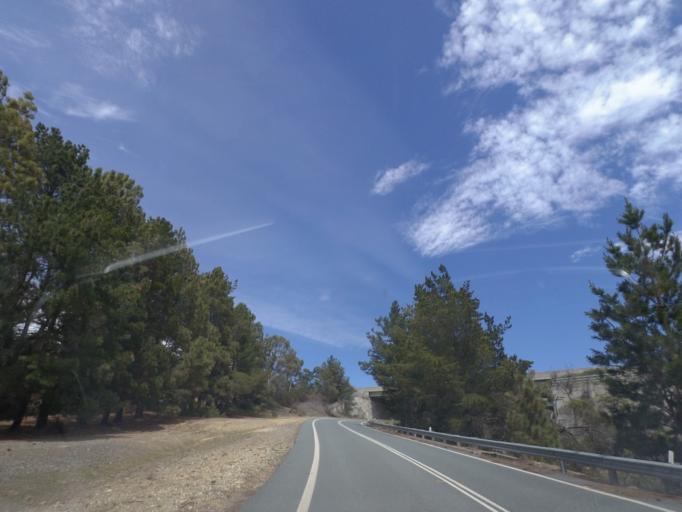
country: AU
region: New South Wales
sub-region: Yass Valley
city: Gundaroo
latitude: -35.1000
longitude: 149.3760
